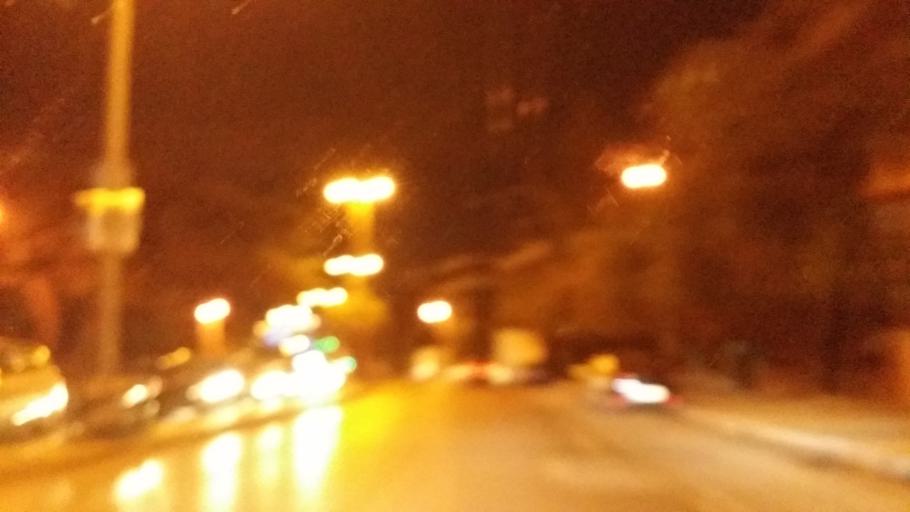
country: GR
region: Attica
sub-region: Nomarchia Athinas
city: Khalandrion
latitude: 38.0211
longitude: 23.7935
